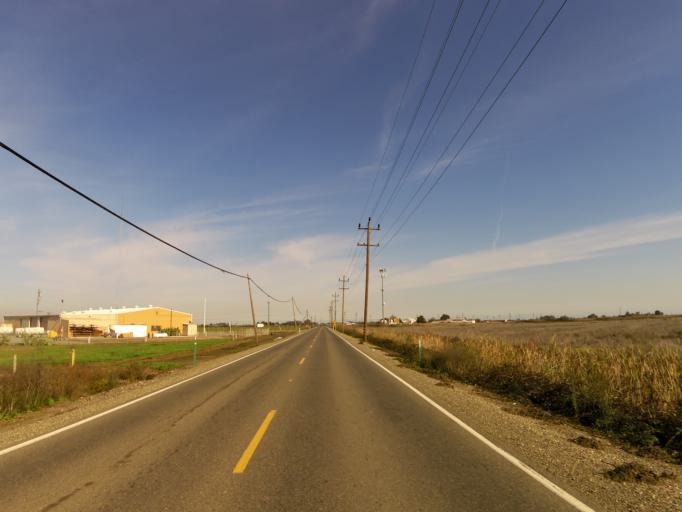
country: US
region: California
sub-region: San Joaquin County
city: Thornton
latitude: 38.2876
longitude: -121.4530
